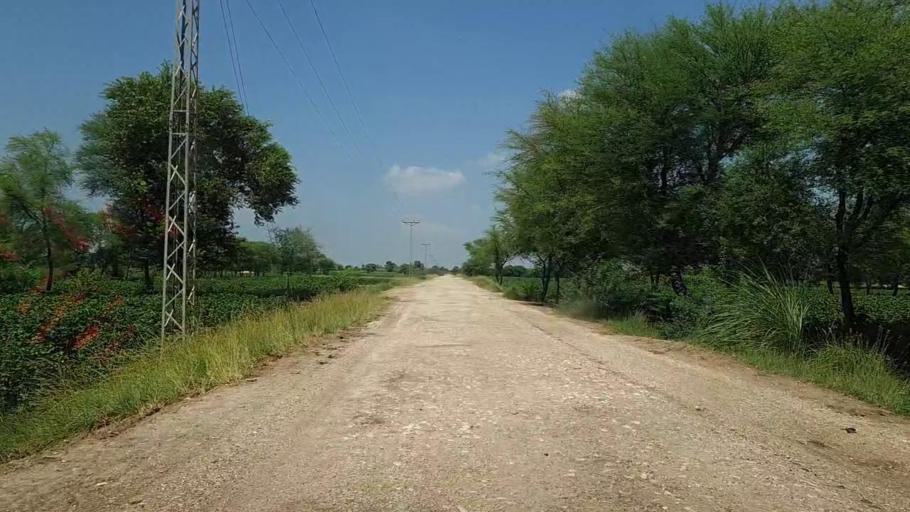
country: PK
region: Sindh
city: Kandiaro
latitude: 26.9936
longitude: 68.2505
